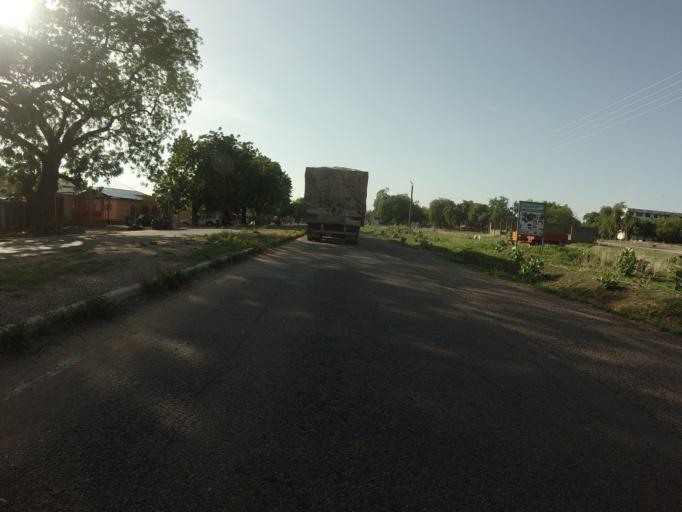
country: GH
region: Upper East
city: Navrongo
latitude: 10.8973
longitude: -1.0919
